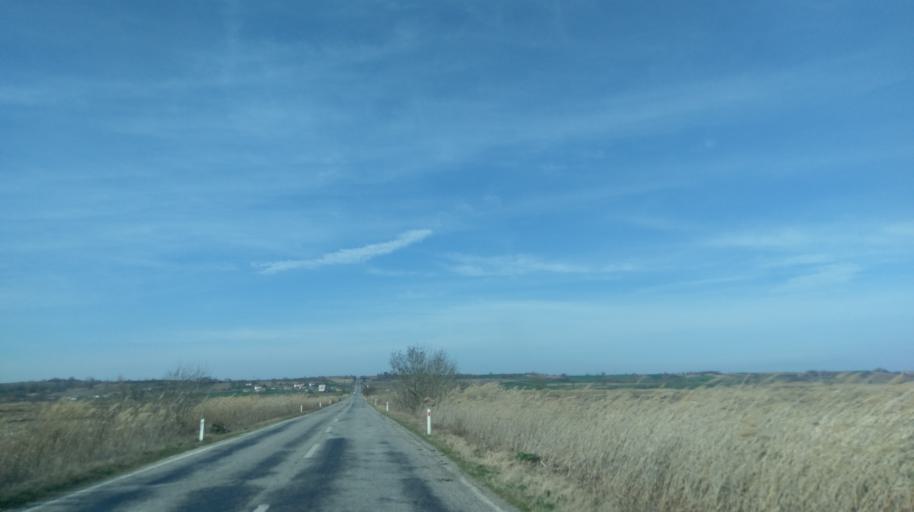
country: TR
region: Edirne
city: Copkoy
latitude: 41.2757
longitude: 26.8056
